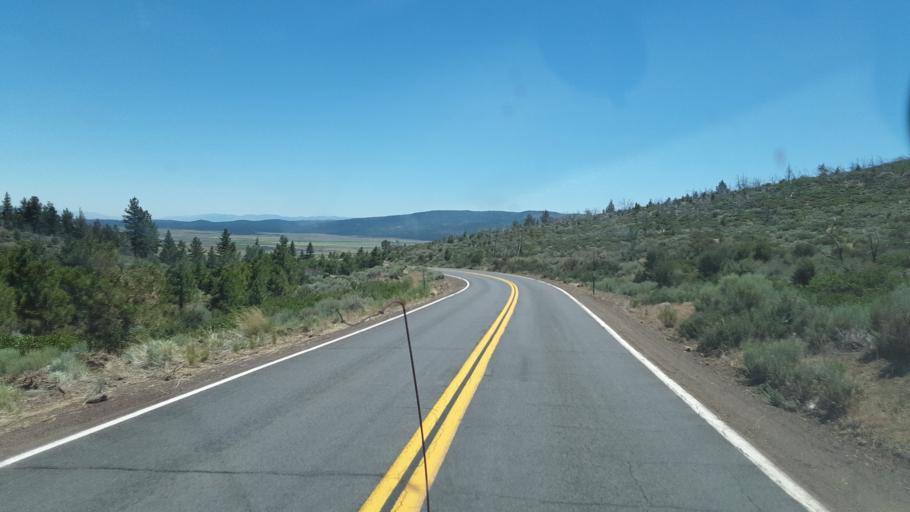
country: US
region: California
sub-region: Lassen County
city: Susanville
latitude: 40.6090
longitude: -120.6432
